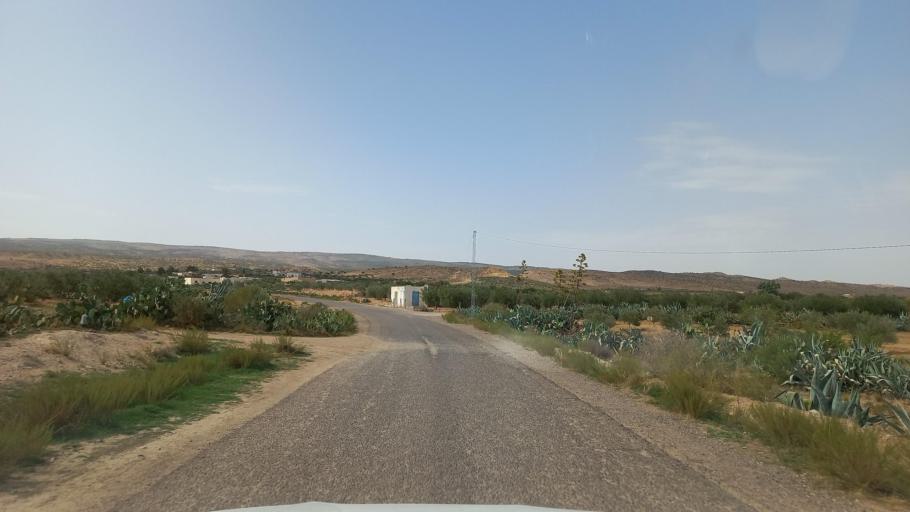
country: TN
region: Al Qasrayn
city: Kasserine
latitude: 35.2984
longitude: 8.9559
